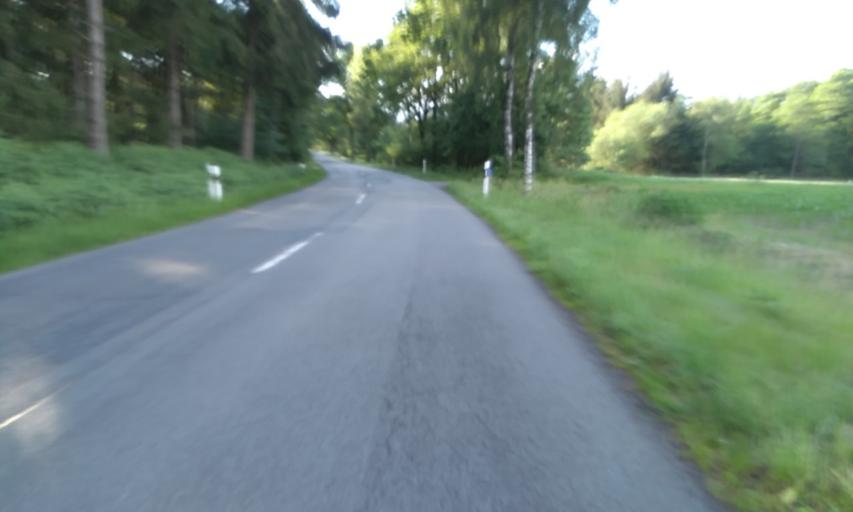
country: DE
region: Lower Saxony
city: Heeslingen
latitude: 53.3556
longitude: 9.3434
